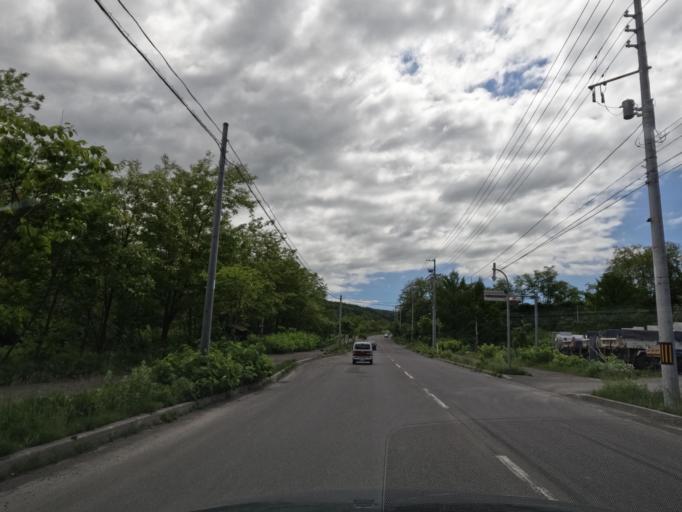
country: JP
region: Hokkaido
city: Bibai
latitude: 43.2589
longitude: 141.9445
